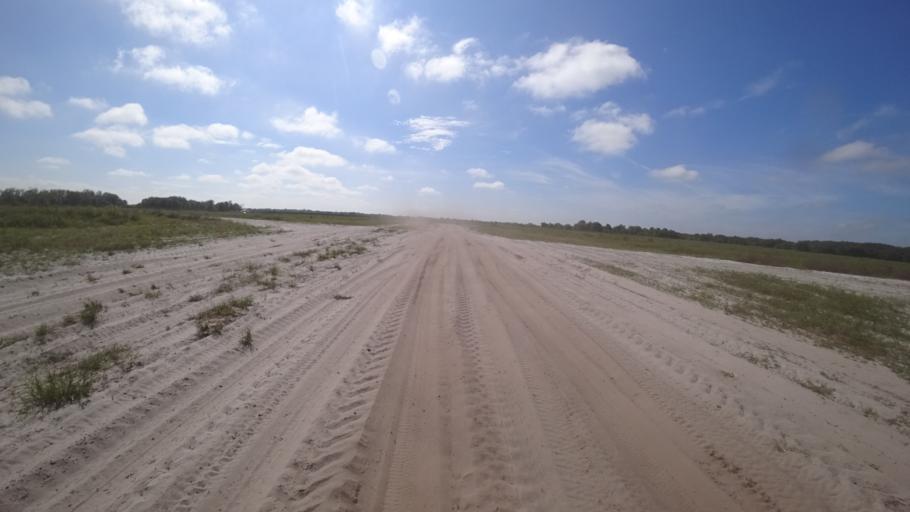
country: US
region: Florida
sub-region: DeSoto County
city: Arcadia
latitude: 27.2902
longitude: -82.0770
